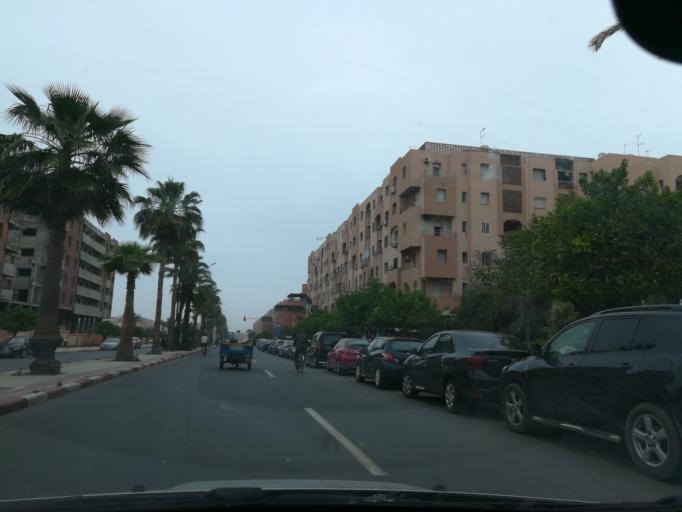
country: MA
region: Marrakech-Tensift-Al Haouz
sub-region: Marrakech
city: Marrakesh
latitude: 31.6599
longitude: -8.0063
